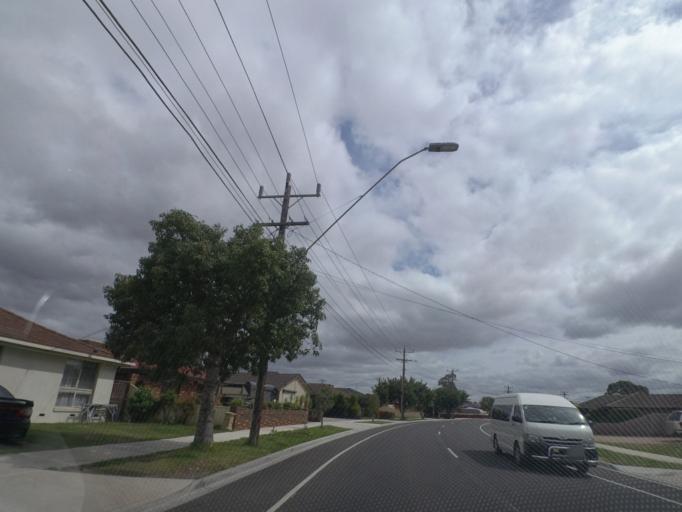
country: AU
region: Victoria
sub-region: Brimbank
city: Deer Park
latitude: -37.7561
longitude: 144.7612
